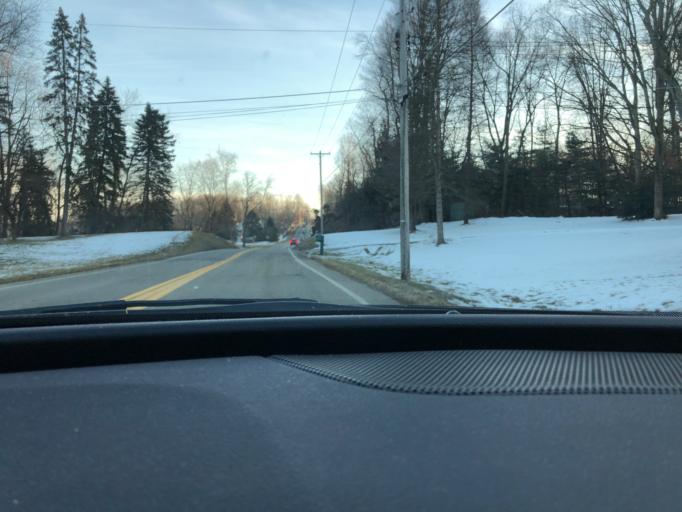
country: US
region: Ohio
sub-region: Stark County
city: Perry Heights
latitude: 40.8107
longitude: -81.4658
